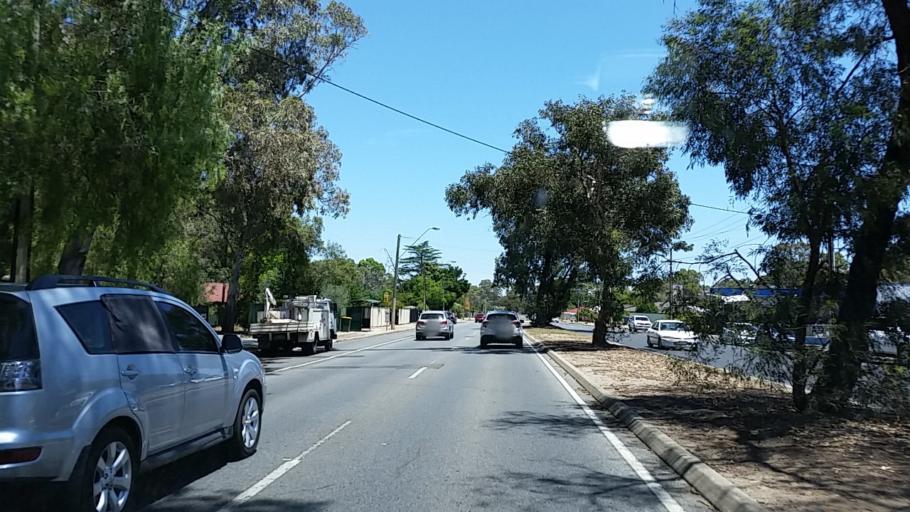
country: AU
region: South Australia
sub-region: Tea Tree Gully
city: Hope Valley
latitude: -34.8233
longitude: 138.7106
